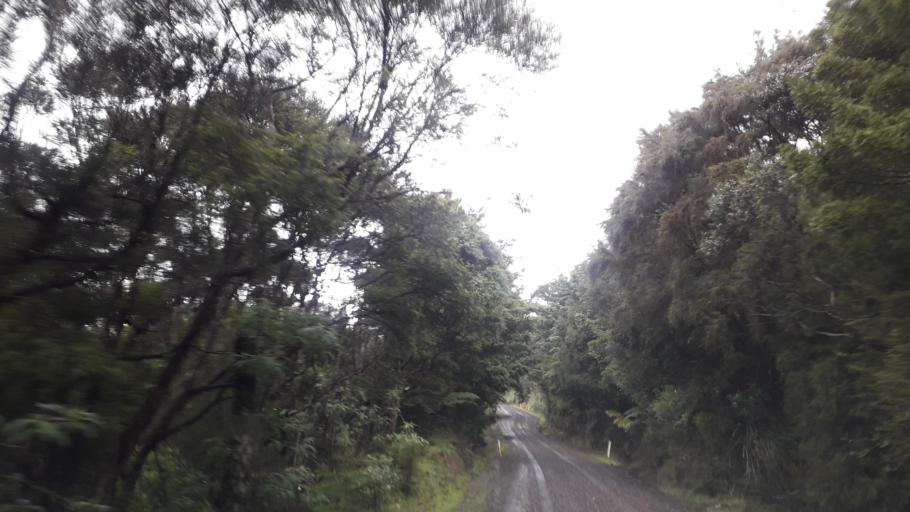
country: NZ
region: Northland
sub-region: Far North District
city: Kaitaia
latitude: -35.3897
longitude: 173.4044
